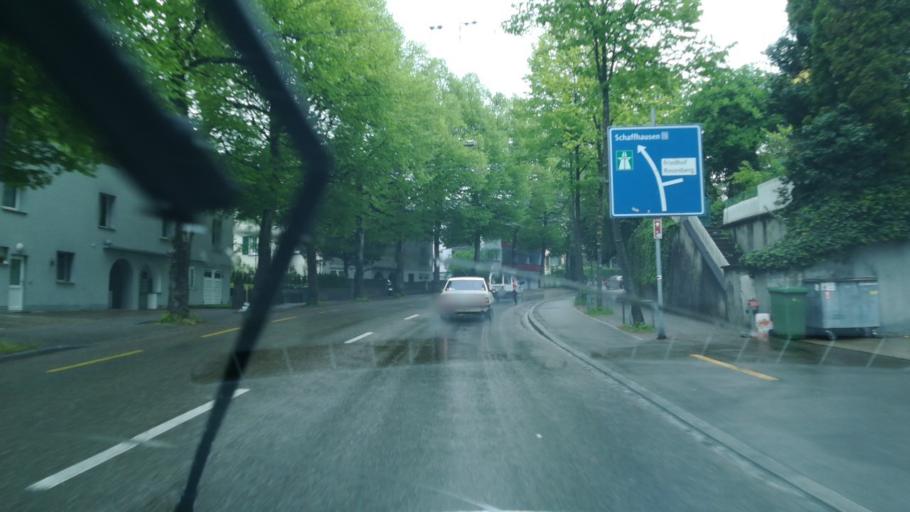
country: CH
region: Zurich
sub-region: Bezirk Winterthur
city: Veltheim
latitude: 47.5118
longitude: 8.7215
